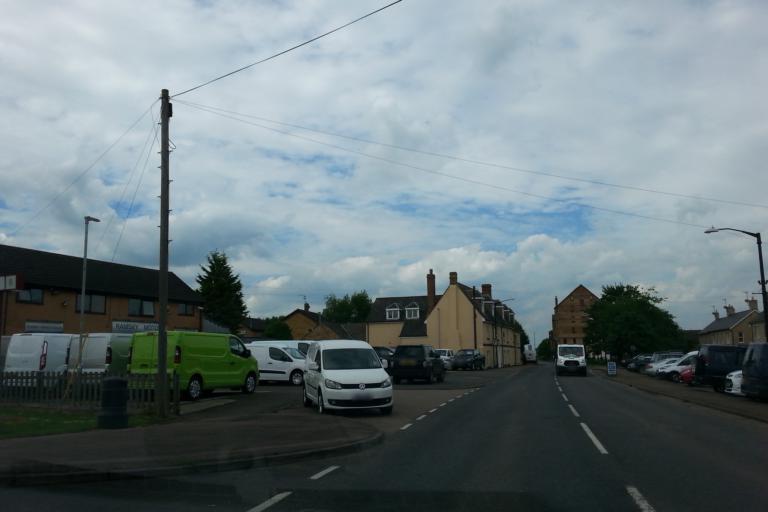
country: GB
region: England
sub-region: Cambridgeshire
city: Ramsey
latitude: 52.4520
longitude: -0.1098
